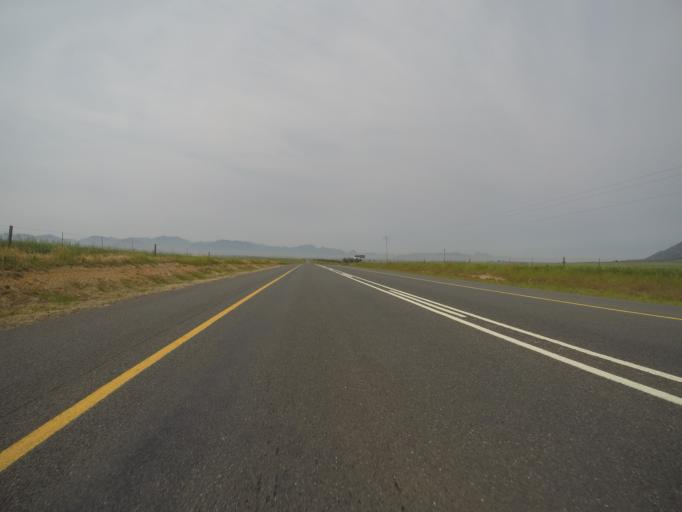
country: ZA
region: Western Cape
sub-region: West Coast District Municipality
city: Malmesbury
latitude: -33.5521
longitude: 18.8703
